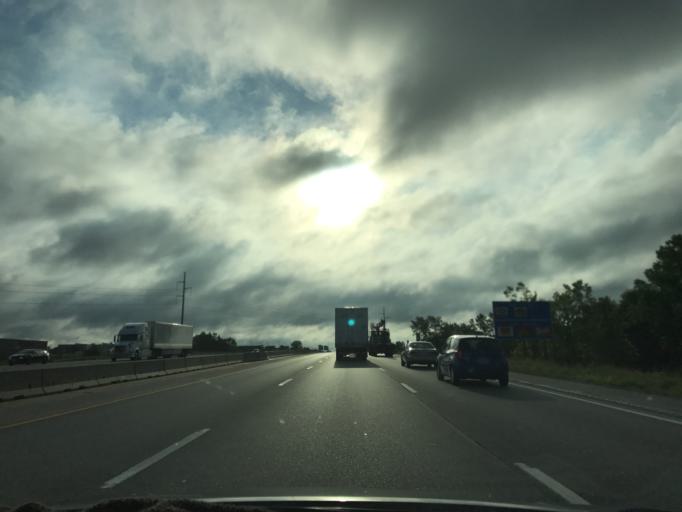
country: US
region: Iowa
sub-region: Johnson County
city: Tiffin
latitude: 41.6942
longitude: -91.6236
